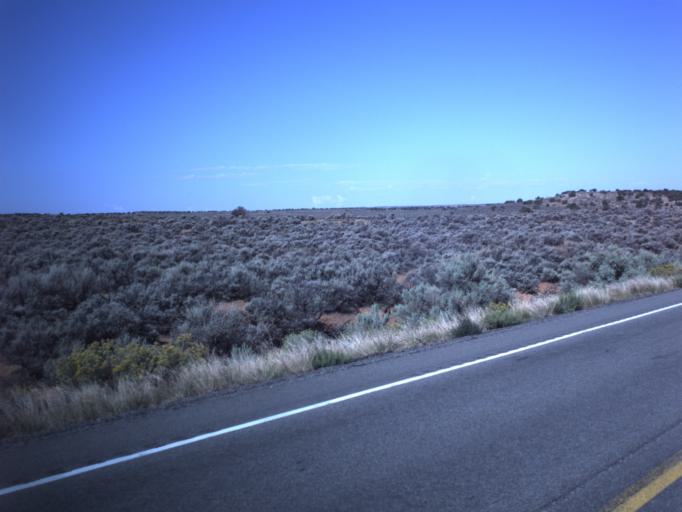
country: US
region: Utah
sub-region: Grand County
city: Moab
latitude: 38.2970
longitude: -109.3883
